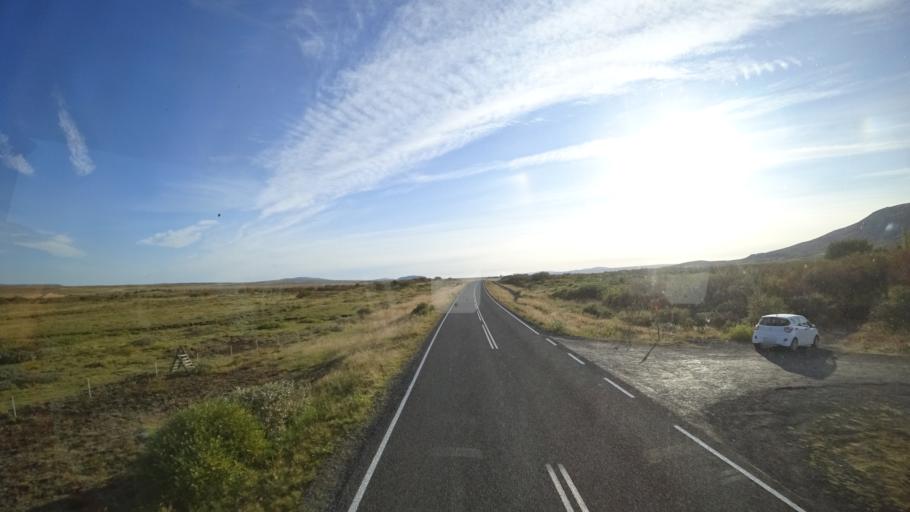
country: IS
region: South
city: Selfoss
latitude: 64.2485
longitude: -20.4941
